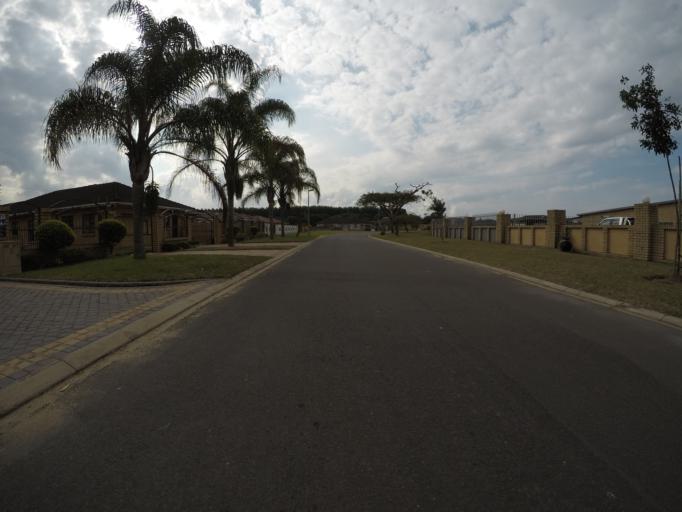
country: ZA
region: KwaZulu-Natal
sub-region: uThungulu District Municipality
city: Richards Bay
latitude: -28.7338
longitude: 32.0864
